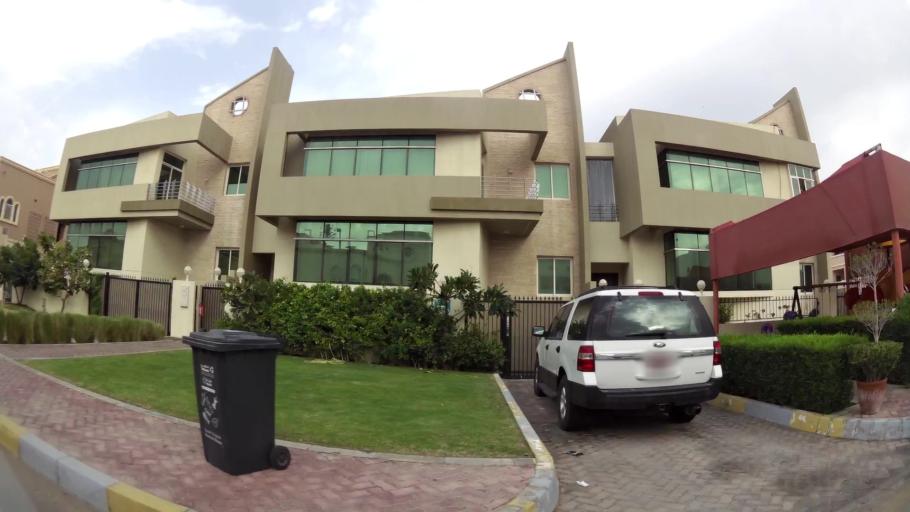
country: AE
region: Abu Dhabi
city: Abu Dhabi
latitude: 24.4740
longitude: 54.3815
